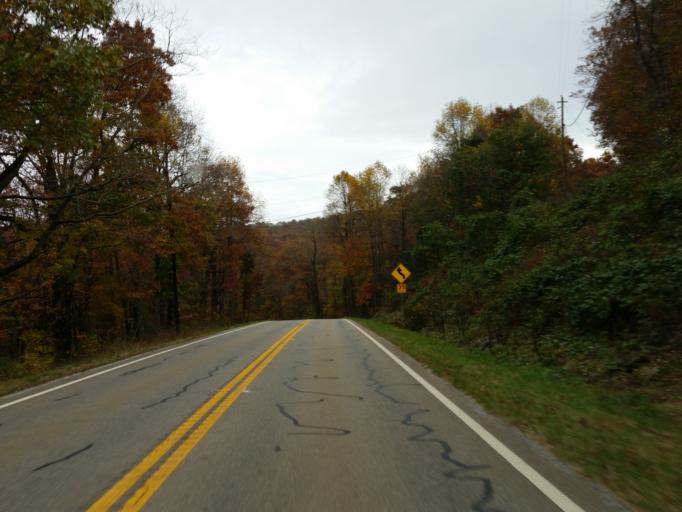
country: US
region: Georgia
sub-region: Pickens County
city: Jasper
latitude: 34.5430
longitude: -84.3681
